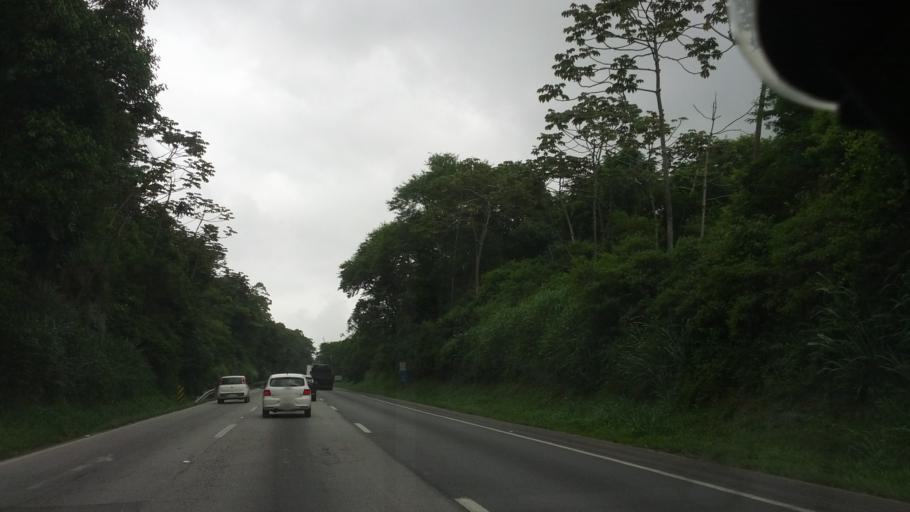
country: BR
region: Santa Catarina
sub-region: Itapema
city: Itapema
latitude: -27.0377
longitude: -48.6004
